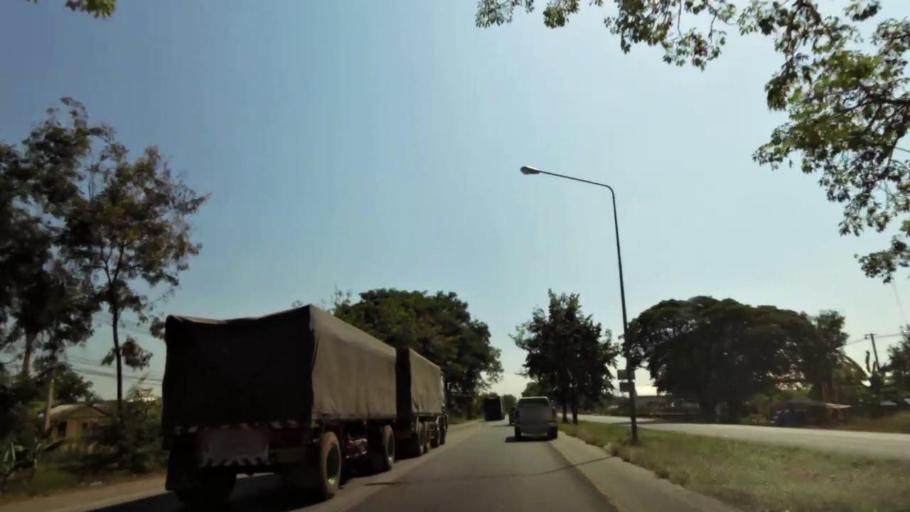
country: TH
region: Nakhon Sawan
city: Kao Liao
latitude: 15.8228
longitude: 100.1193
